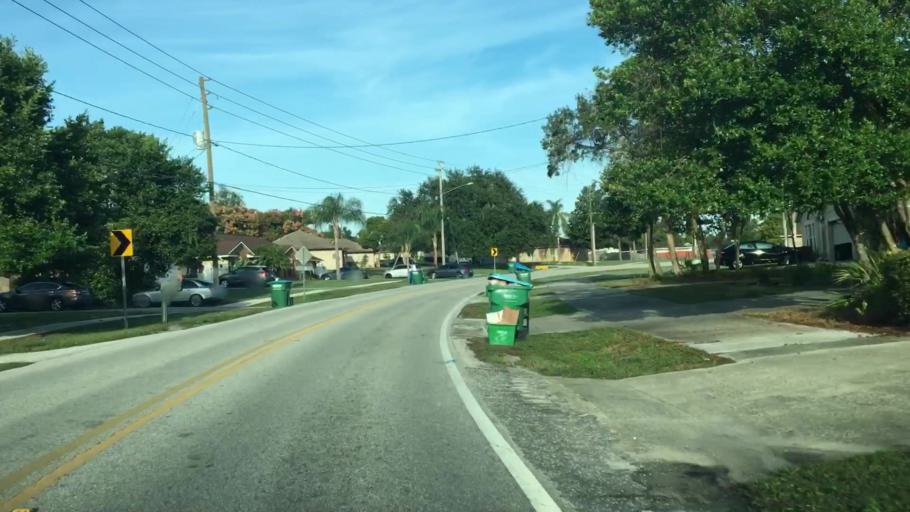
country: US
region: Florida
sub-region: Volusia County
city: Deltona
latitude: 28.9180
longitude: -81.2360
